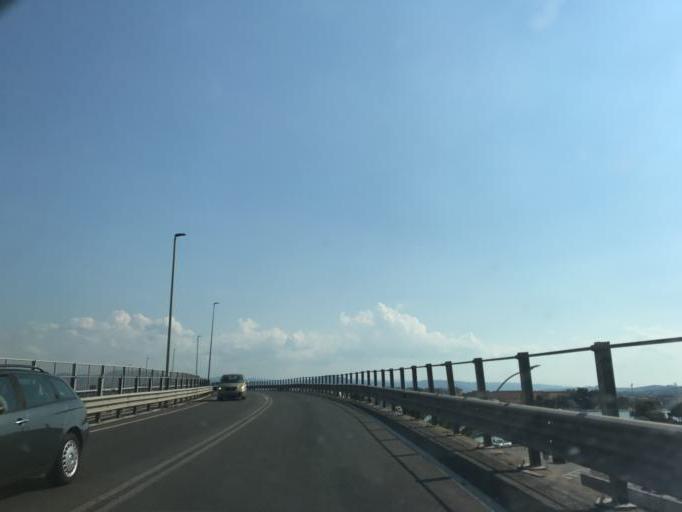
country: IT
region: Sardinia
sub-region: Provincia di Olbia-Tempio
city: Olbia
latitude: 40.9207
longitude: 9.5019
